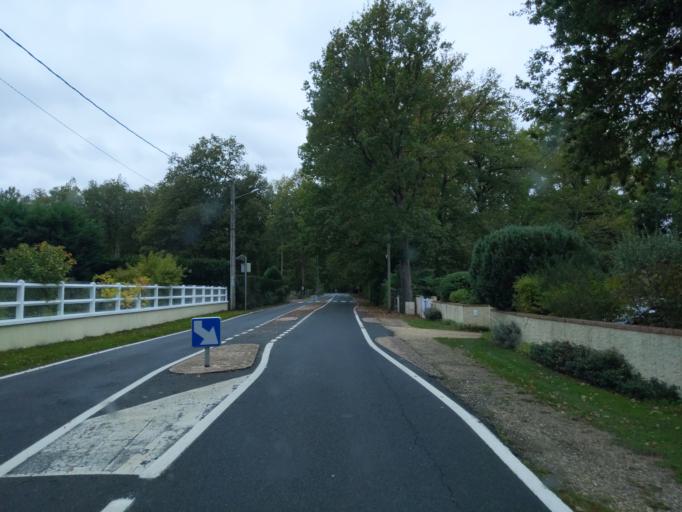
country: FR
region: Ile-de-France
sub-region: Departement des Yvelines
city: Bullion
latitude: 48.6104
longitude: 1.9680
